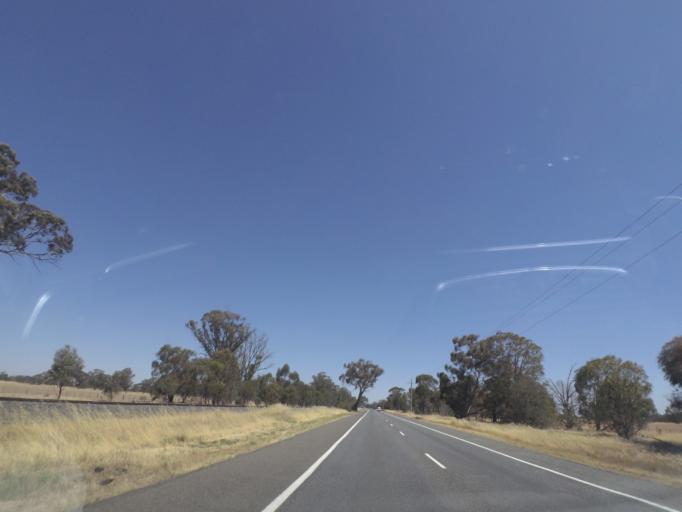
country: AU
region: Victoria
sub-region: Greater Shepparton
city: Shepparton
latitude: -36.2246
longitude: 145.4318
